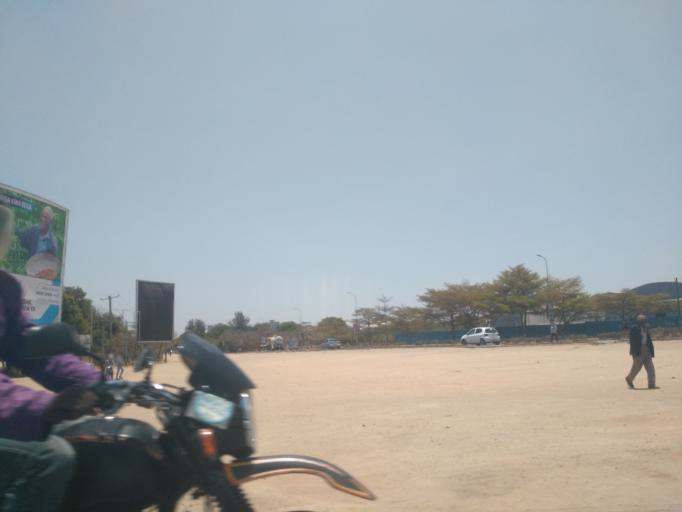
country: TZ
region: Dodoma
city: Dodoma
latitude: -6.1811
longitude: 35.7522
